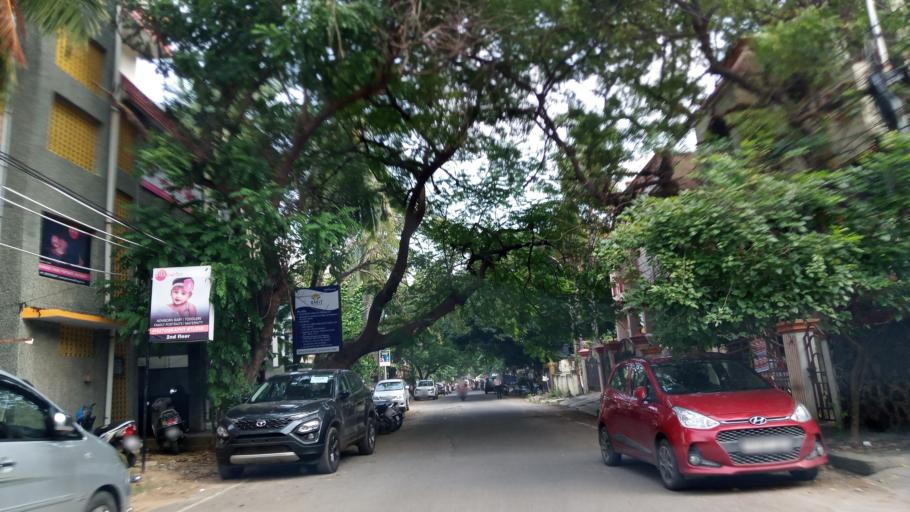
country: IN
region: Tamil Nadu
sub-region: Kancheepuram
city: Alandur
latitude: 13.0387
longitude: 80.2178
